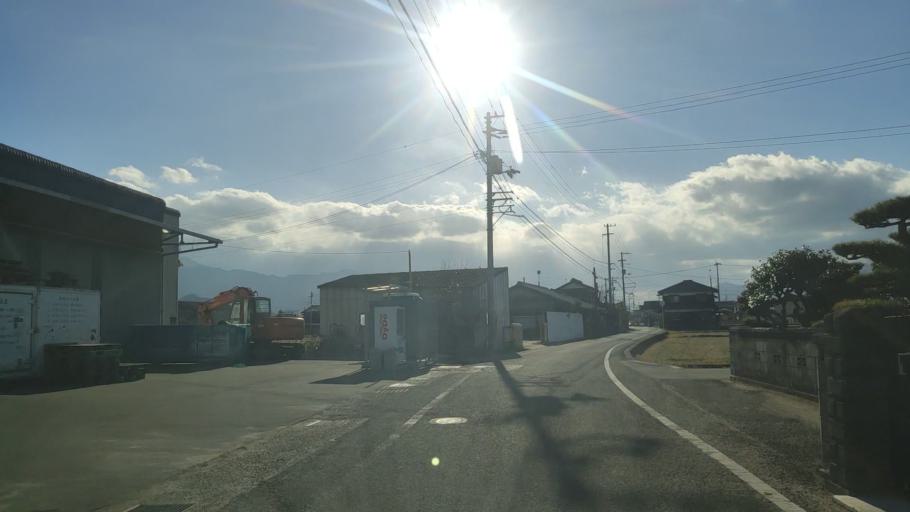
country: JP
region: Ehime
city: Saijo
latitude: 33.9119
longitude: 133.0986
